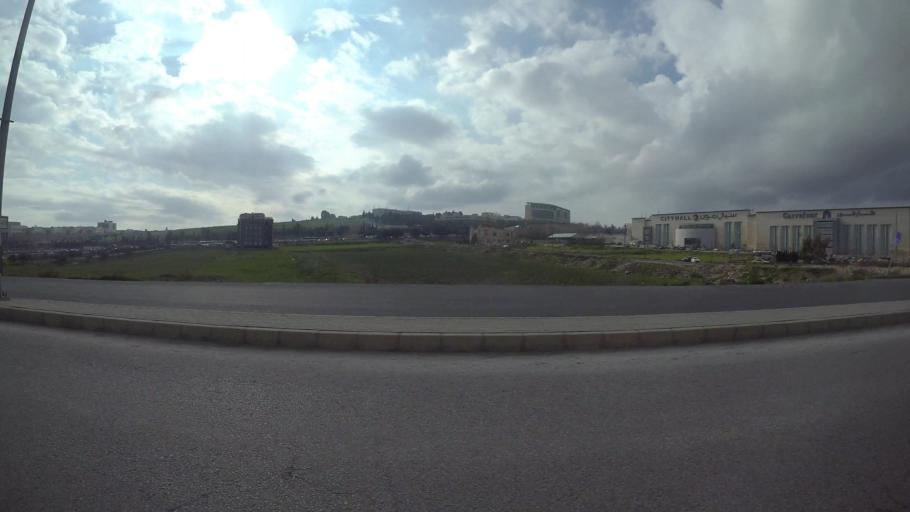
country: JO
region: Amman
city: Wadi as Sir
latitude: 31.9782
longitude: 35.8406
